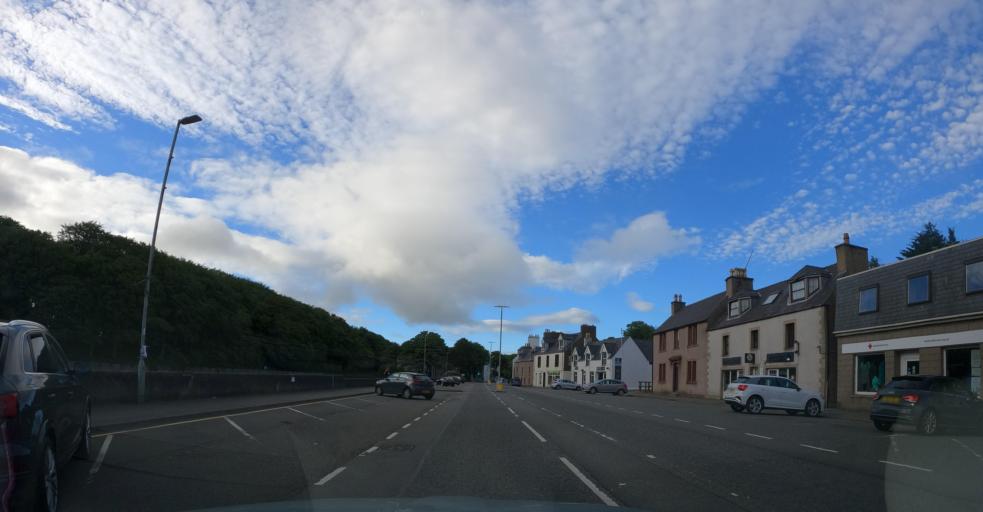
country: GB
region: Scotland
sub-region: Eilean Siar
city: Stornoway
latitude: 58.2117
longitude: -6.3883
